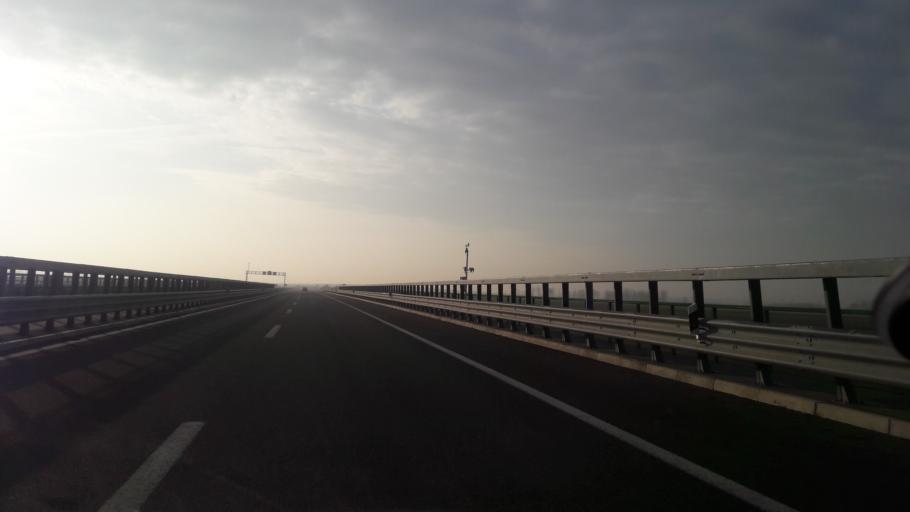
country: HR
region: Osjecko-Baranjska
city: Gorjani
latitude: 45.3649
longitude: 18.3970
